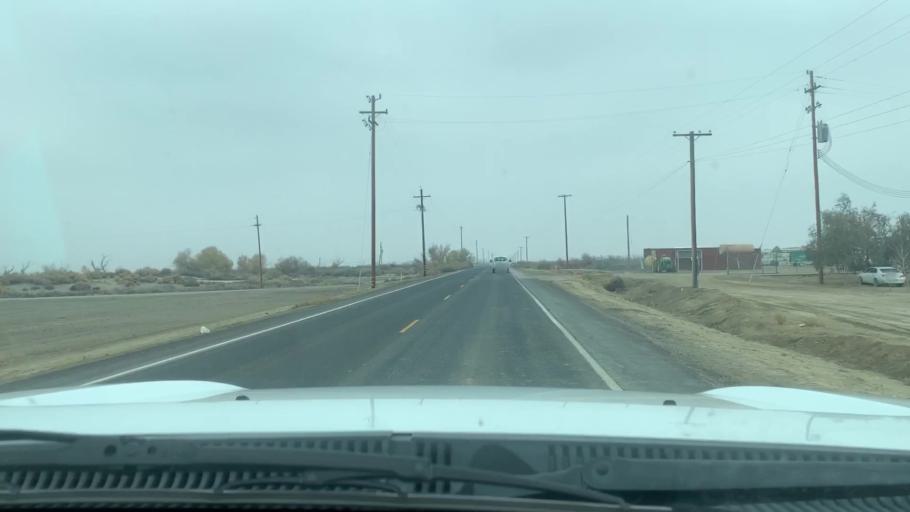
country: US
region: California
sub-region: Kern County
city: Lost Hills
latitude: 35.4994
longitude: -119.6210
